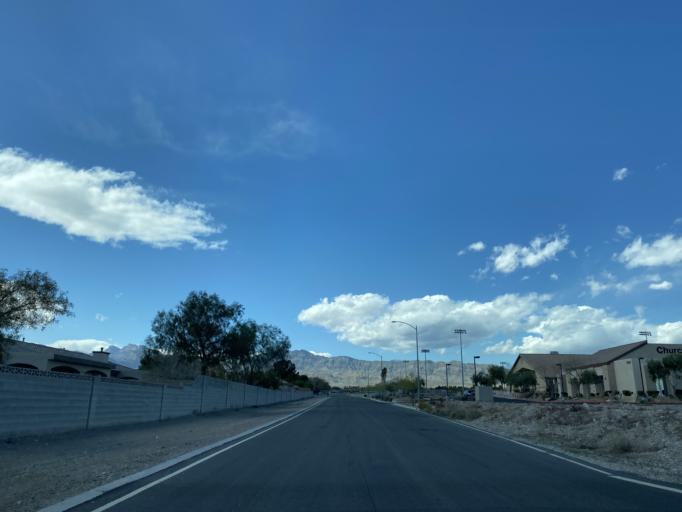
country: US
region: Nevada
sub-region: Clark County
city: Summerlin South
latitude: 36.2719
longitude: -115.2813
